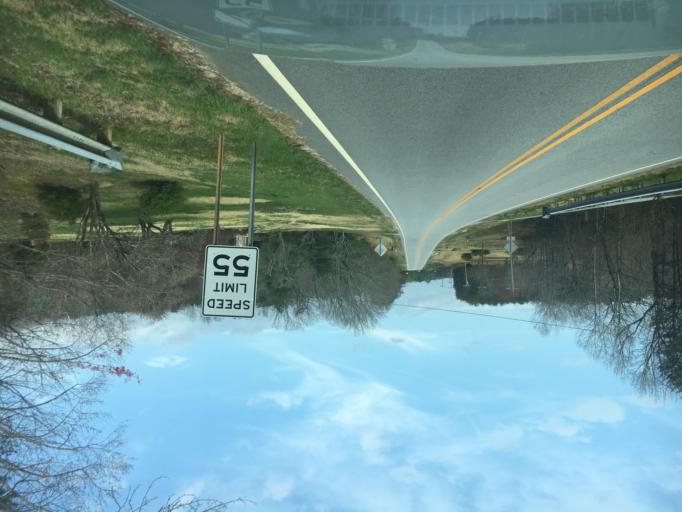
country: US
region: South Carolina
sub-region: Greenville County
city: Tigerville
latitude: 35.1208
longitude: -82.3358
